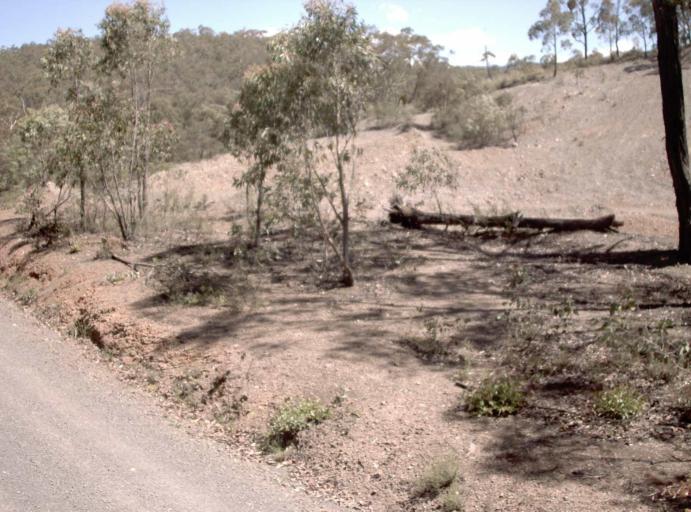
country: AU
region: New South Wales
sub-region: Bombala
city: Bombala
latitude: -37.1012
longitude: 148.6359
